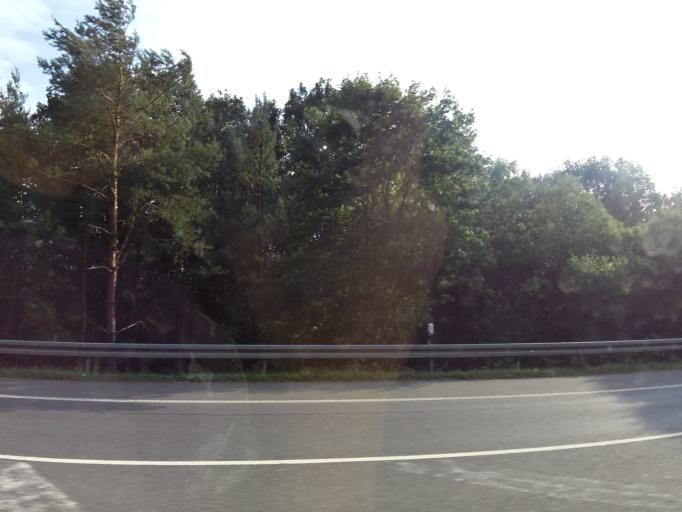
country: DE
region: Hesse
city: Morfelden-Walldorf
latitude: 50.0329
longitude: 8.6011
